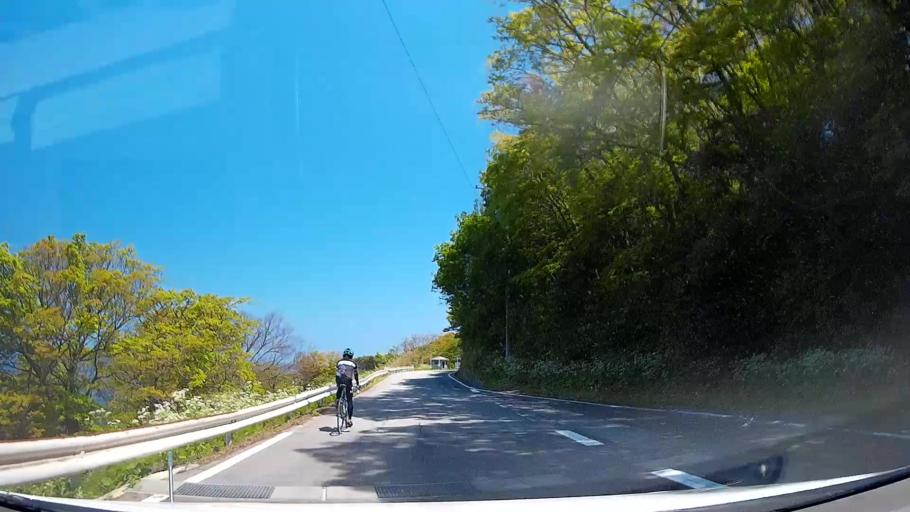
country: JP
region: Ishikawa
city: Nanao
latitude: 37.5256
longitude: 137.2659
